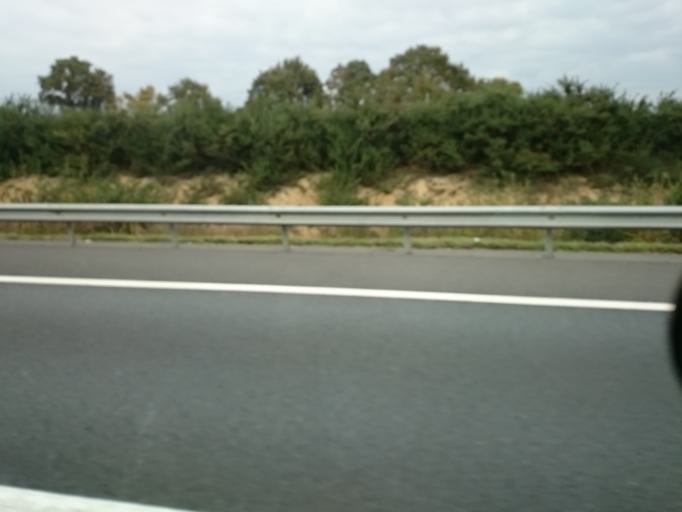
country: FR
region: Pays de la Loire
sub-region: Departement de la Loire-Atlantique
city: Sautron
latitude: 47.2627
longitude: -1.7037
